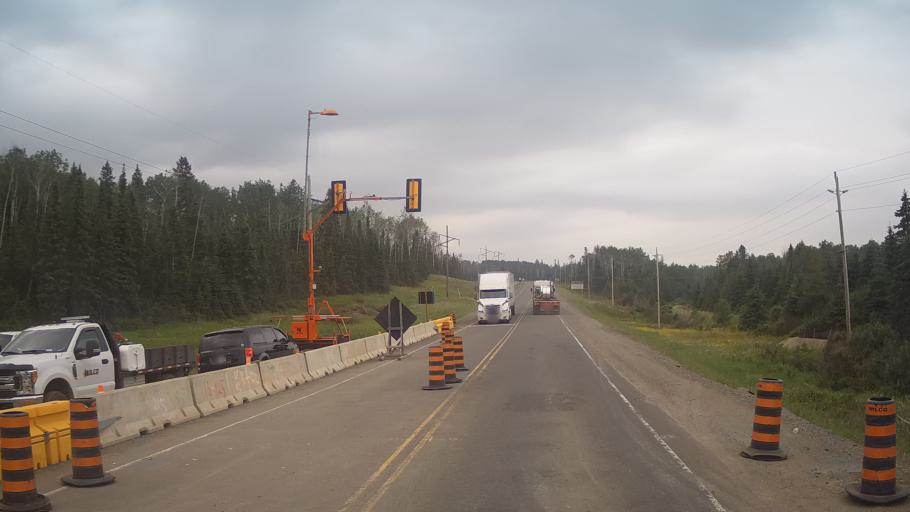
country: CA
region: Ontario
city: Greenstone
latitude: 49.5834
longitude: -87.9706
